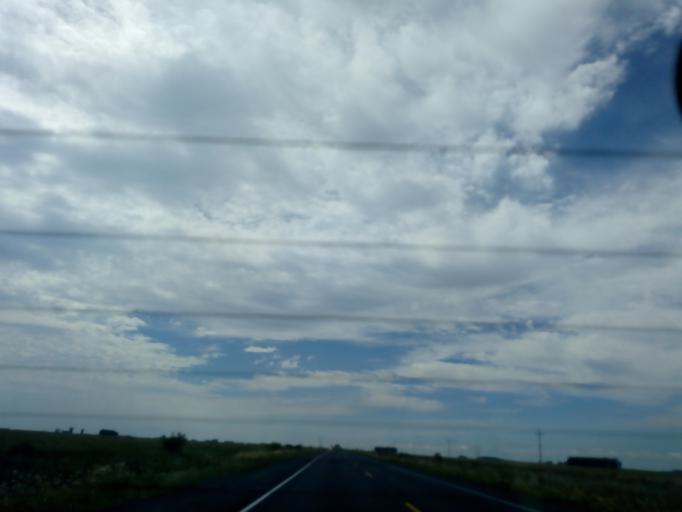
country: BR
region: Rio Grande do Sul
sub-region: Quarai
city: Quarai
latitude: -29.9808
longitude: -56.5427
